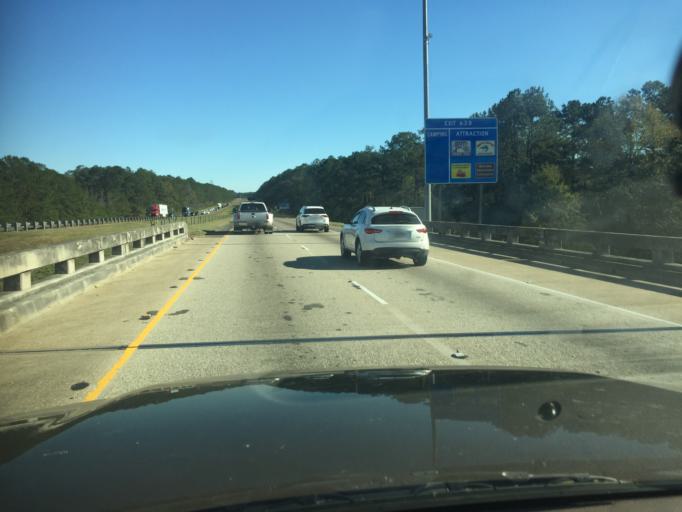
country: US
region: Louisiana
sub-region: Saint Tammany Parish
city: Covington
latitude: 30.4393
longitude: -90.1178
